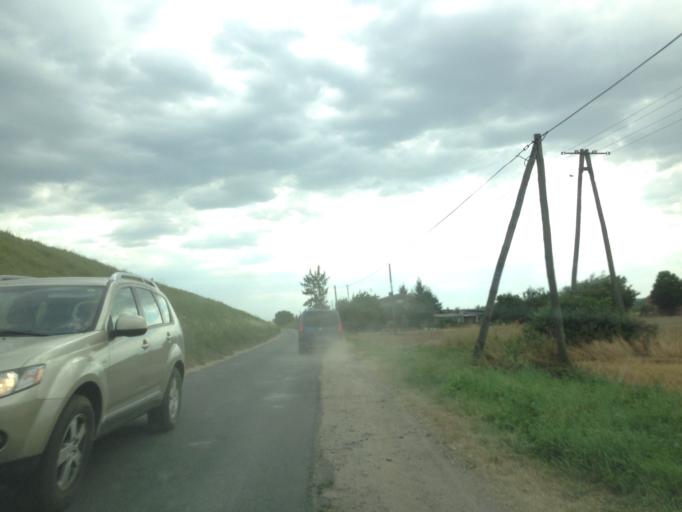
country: PL
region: Kujawsko-Pomorskie
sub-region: Powiat chelminski
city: Chelmno
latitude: 53.3475
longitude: 18.3583
